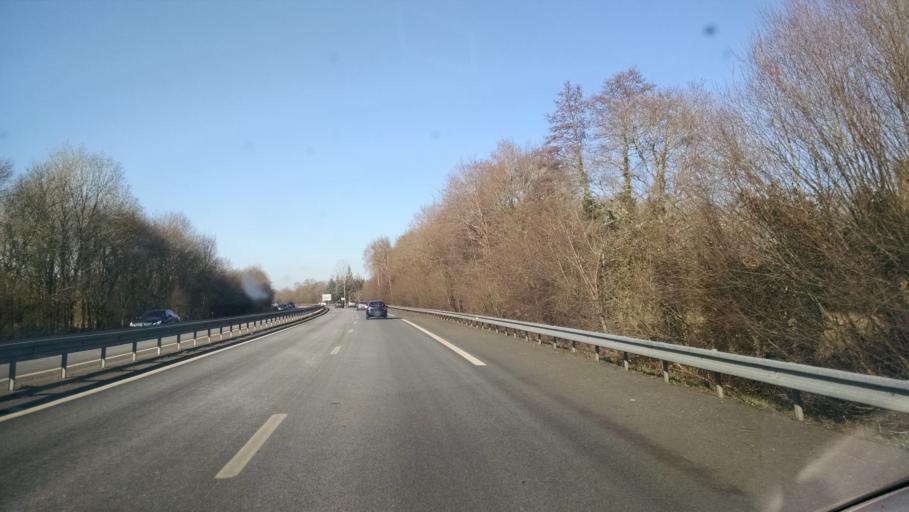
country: FR
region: Brittany
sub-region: Departement du Morbihan
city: Landevant
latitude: 47.7532
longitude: -3.1109
